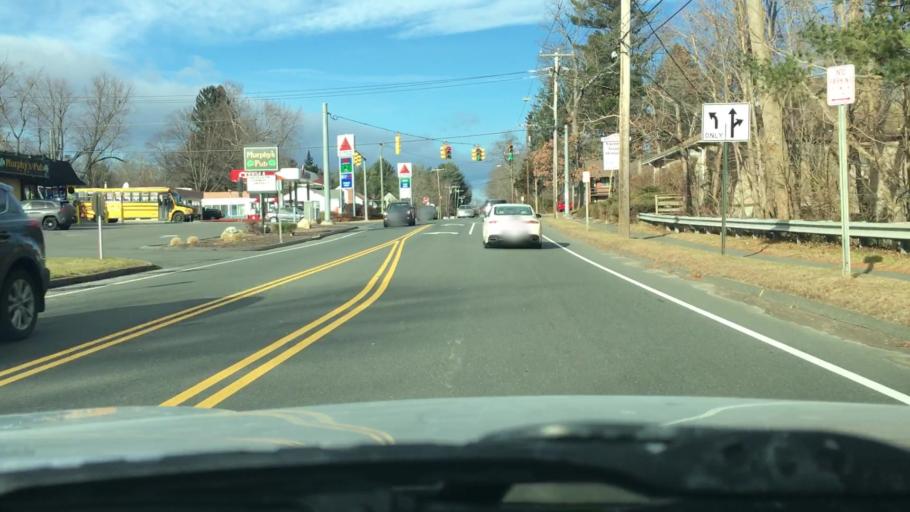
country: US
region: Massachusetts
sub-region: Hampden County
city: Agawam
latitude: 42.0666
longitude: -72.6315
